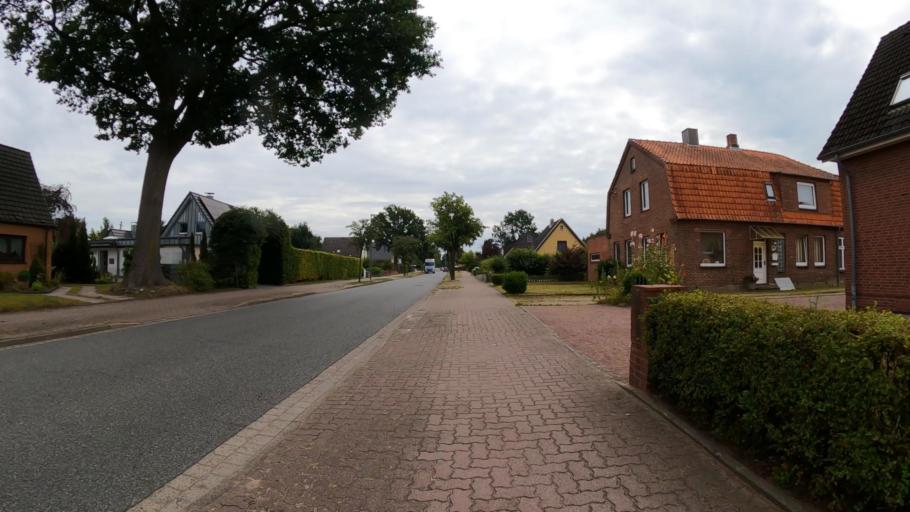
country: DE
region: Schleswig-Holstein
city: Boostedt
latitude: 54.0524
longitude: 10.0285
